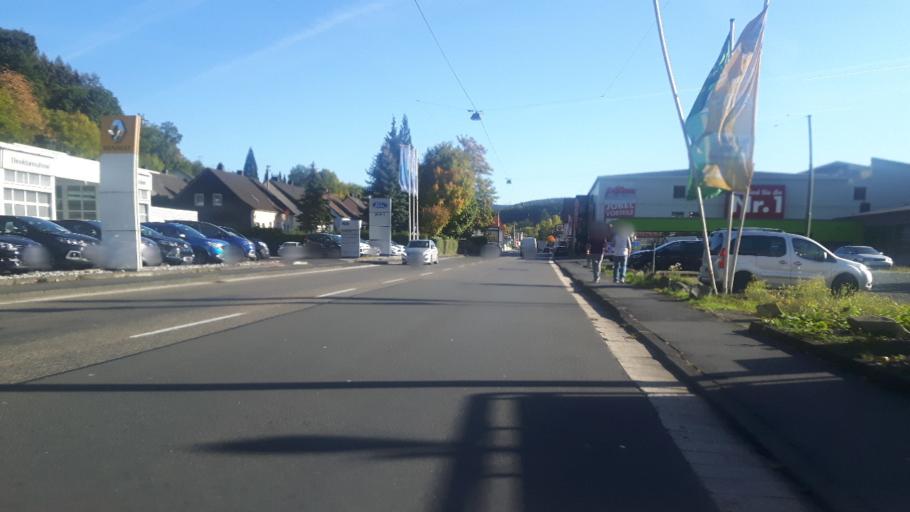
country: DE
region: Rheinland-Pfalz
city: Betzdorf
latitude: 50.7980
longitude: 7.8615
